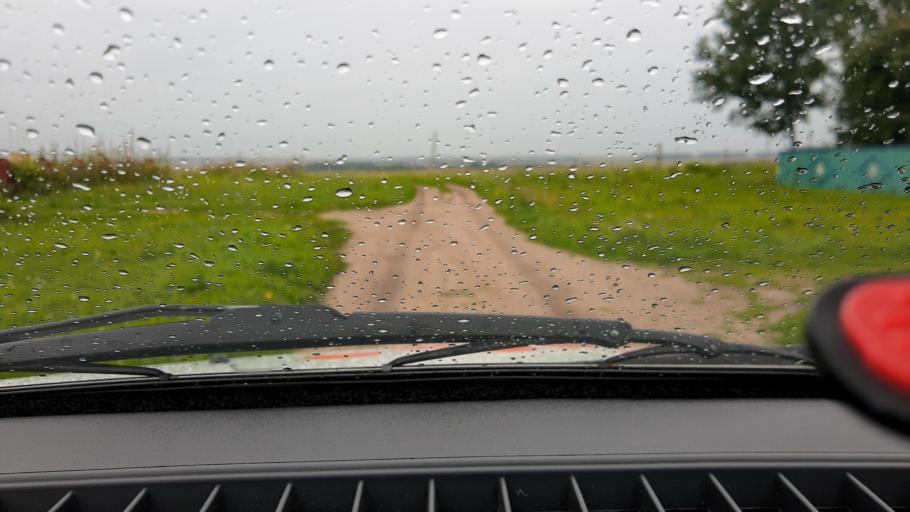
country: RU
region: Bashkortostan
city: Karmaskaly
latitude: 54.3781
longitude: 56.1126
